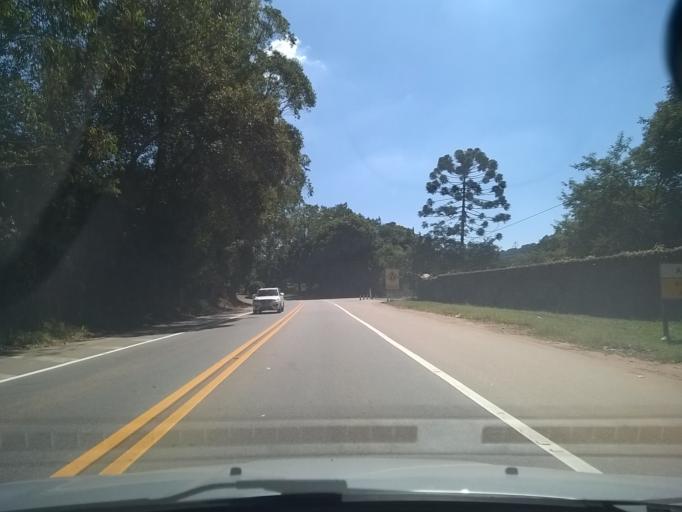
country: BR
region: Sao Paulo
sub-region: Varzea Paulista
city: Varzea Paulista
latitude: -23.2545
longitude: -46.8360
